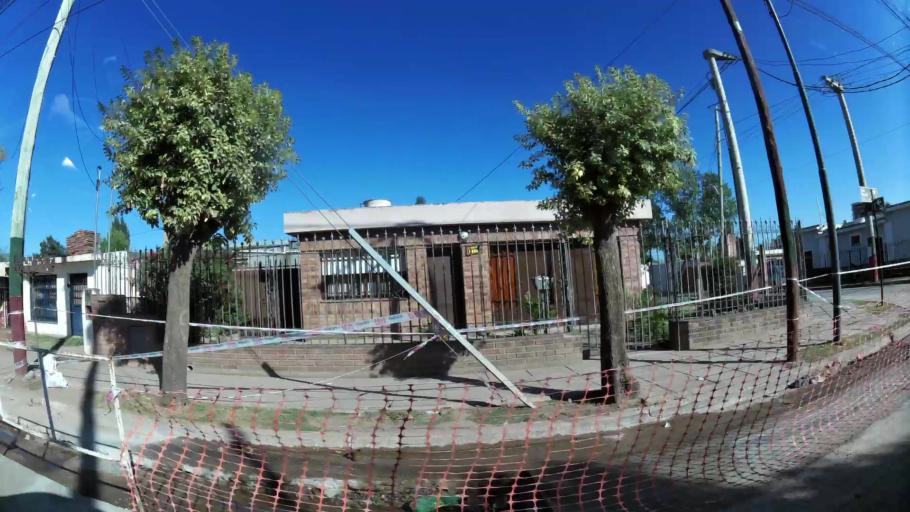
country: AR
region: Cordoba
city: Villa Allende
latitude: -31.3280
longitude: -64.2611
